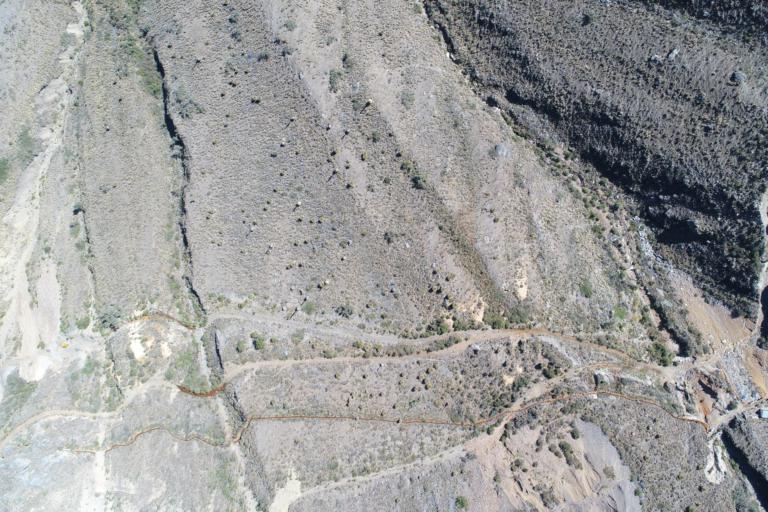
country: BO
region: La Paz
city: Viloco
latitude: -16.8086
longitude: -67.5539
